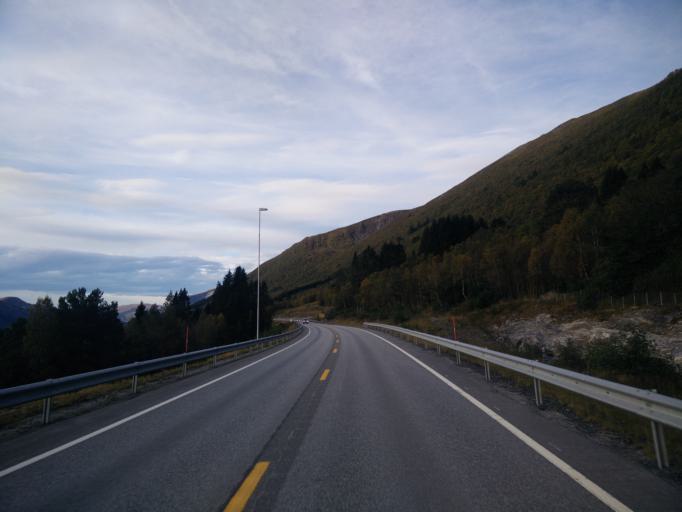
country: NO
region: More og Romsdal
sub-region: Gjemnes
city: Batnfjordsora
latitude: 62.9509
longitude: 7.7607
